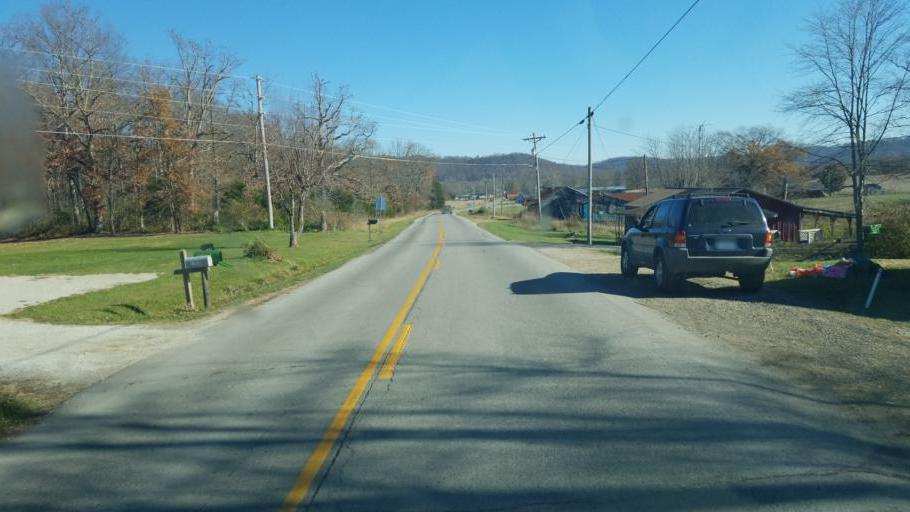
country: US
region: Kentucky
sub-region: Fleming County
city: Flemingsburg
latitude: 38.4772
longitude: -83.6022
